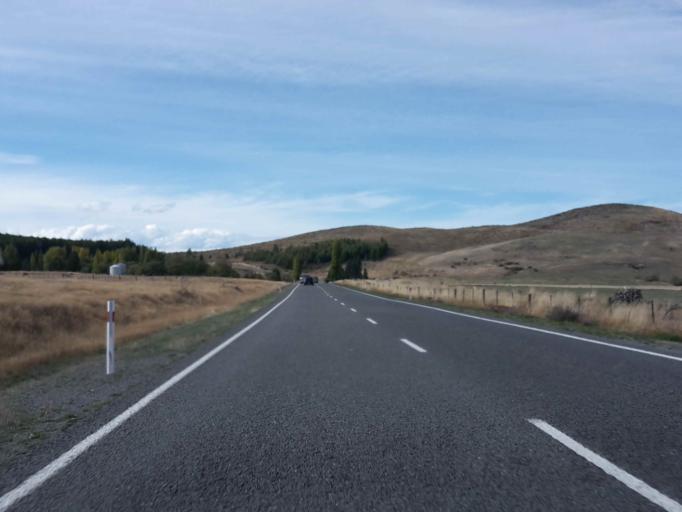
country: NZ
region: Canterbury
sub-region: Timaru District
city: Pleasant Point
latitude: -44.2031
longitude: 170.2672
